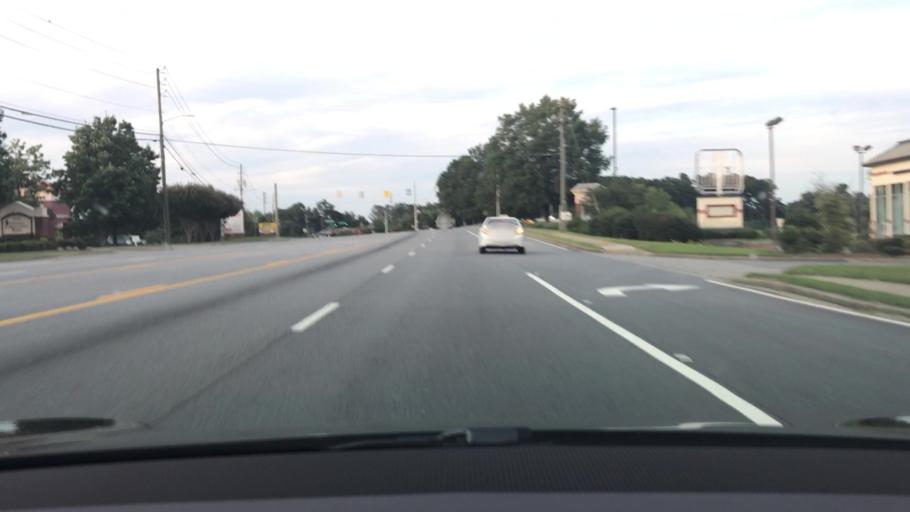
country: US
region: Georgia
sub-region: Gwinnett County
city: Duluth
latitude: 34.0073
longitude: -84.1334
